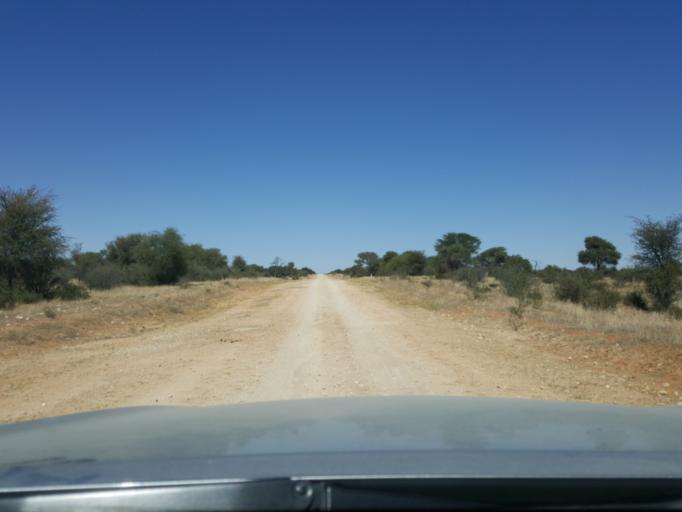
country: BW
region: Kgalagadi
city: Hukuntsi
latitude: -24.0443
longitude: 21.2200
